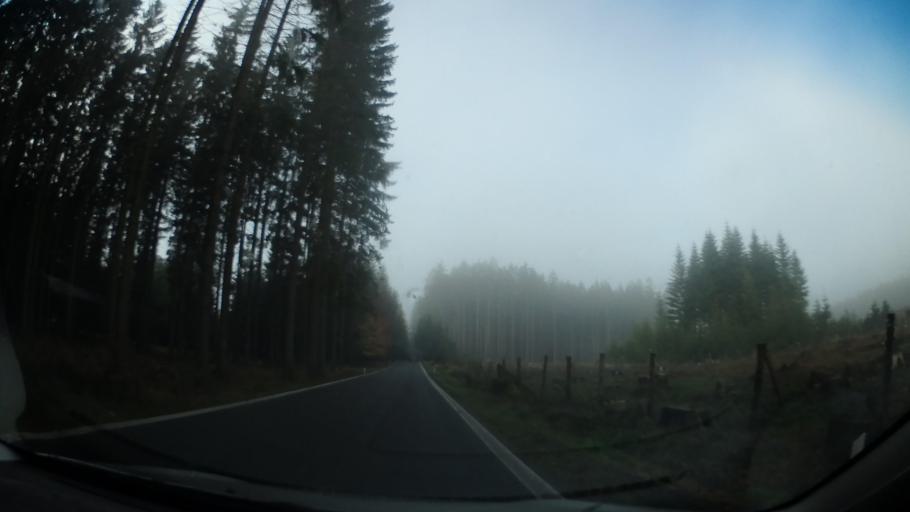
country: CZ
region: Vysocina
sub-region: Okres Zd'ar nad Sazavou
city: Nove Mesto na Morave
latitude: 49.4788
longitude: 16.0374
